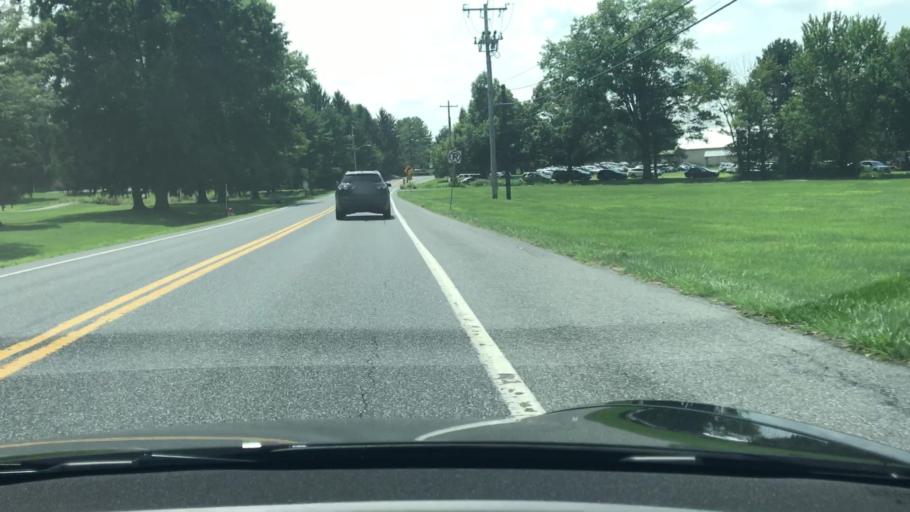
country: US
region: Pennsylvania
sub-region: Lancaster County
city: Landisville
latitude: 40.0703
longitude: -76.4105
